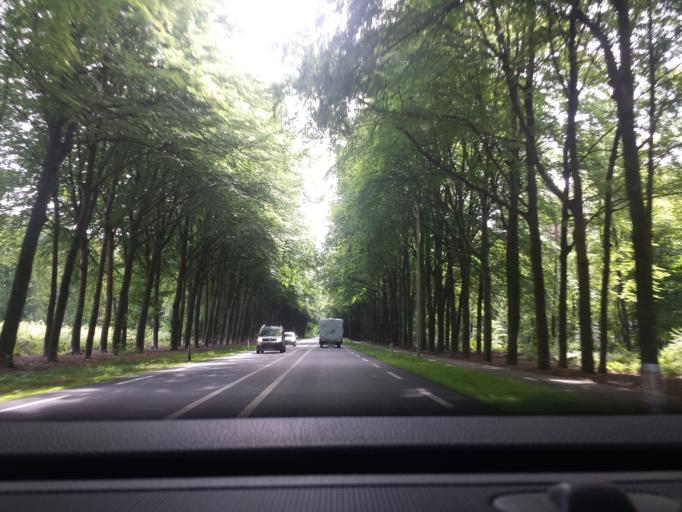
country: NL
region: Gelderland
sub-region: Gemeente Lochem
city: Barchem
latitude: 52.0825
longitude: 6.4211
